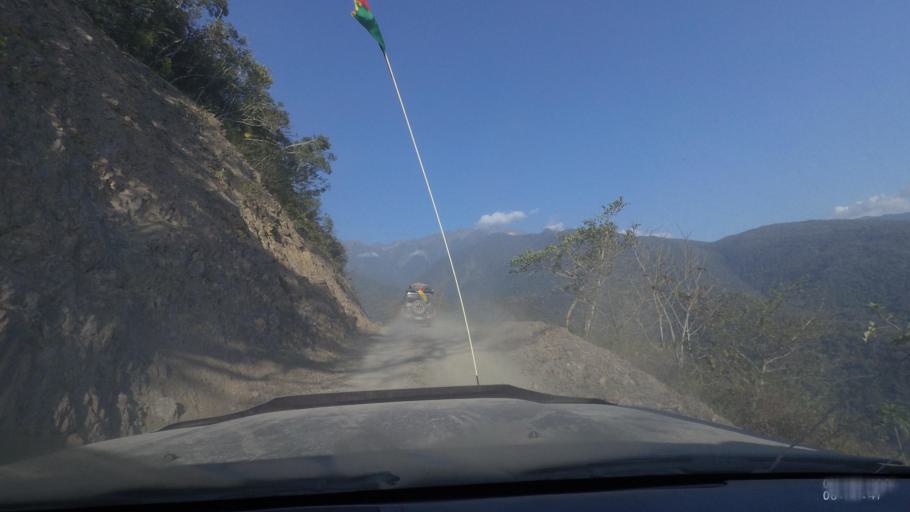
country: BO
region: La Paz
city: Quime
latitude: -16.5169
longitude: -66.7676
